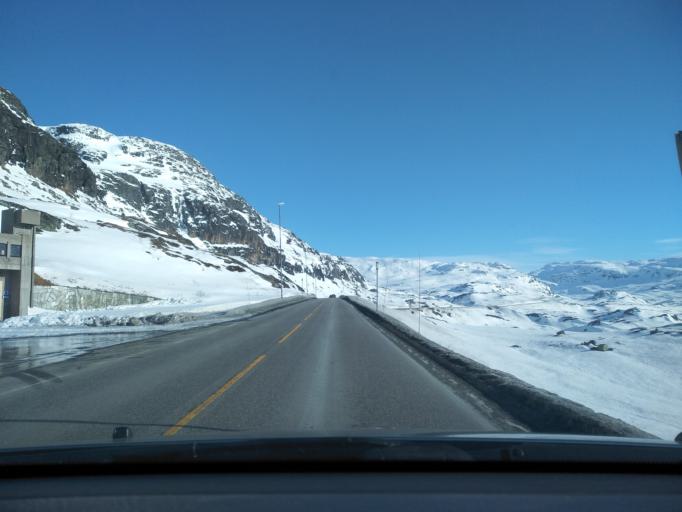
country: NO
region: Hordaland
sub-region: Odda
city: Odda
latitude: 59.8492
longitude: 6.9528
